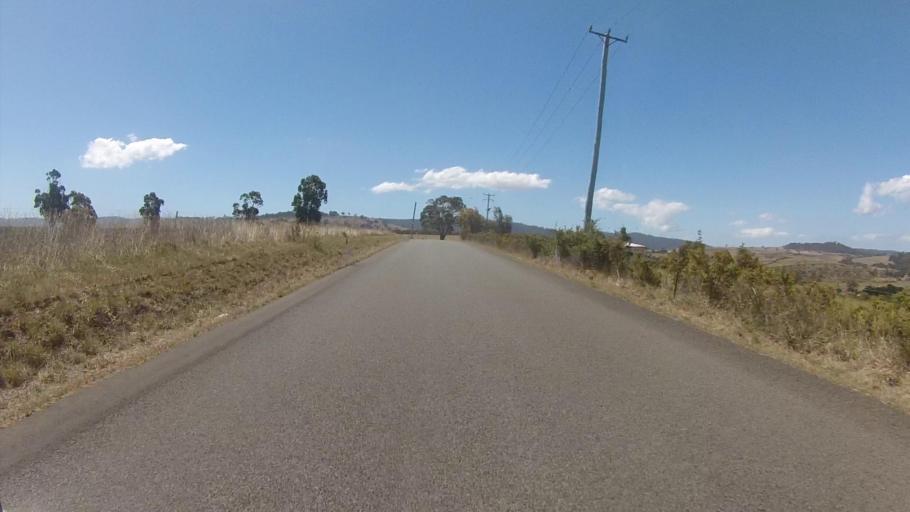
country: AU
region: Tasmania
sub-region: Sorell
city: Sorell
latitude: -42.7746
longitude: 147.5810
